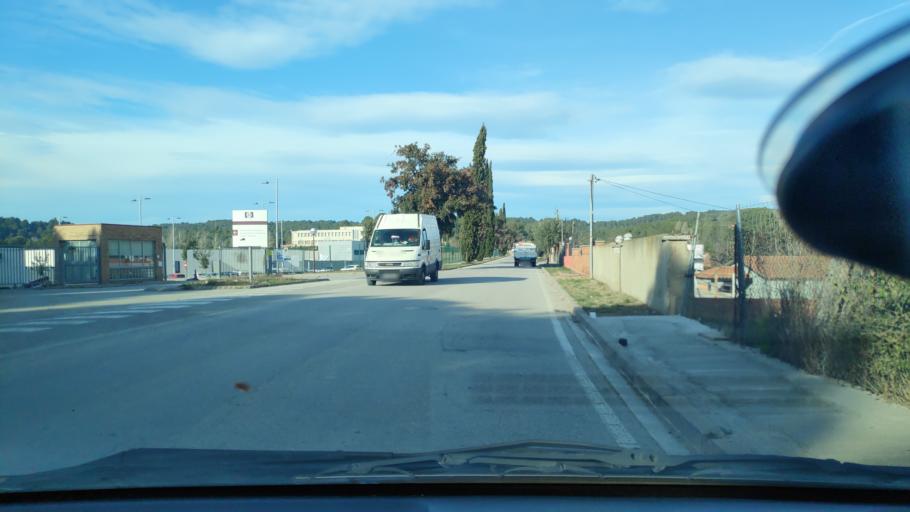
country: ES
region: Catalonia
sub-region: Provincia de Barcelona
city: Rubi
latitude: 41.4939
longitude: 2.0654
